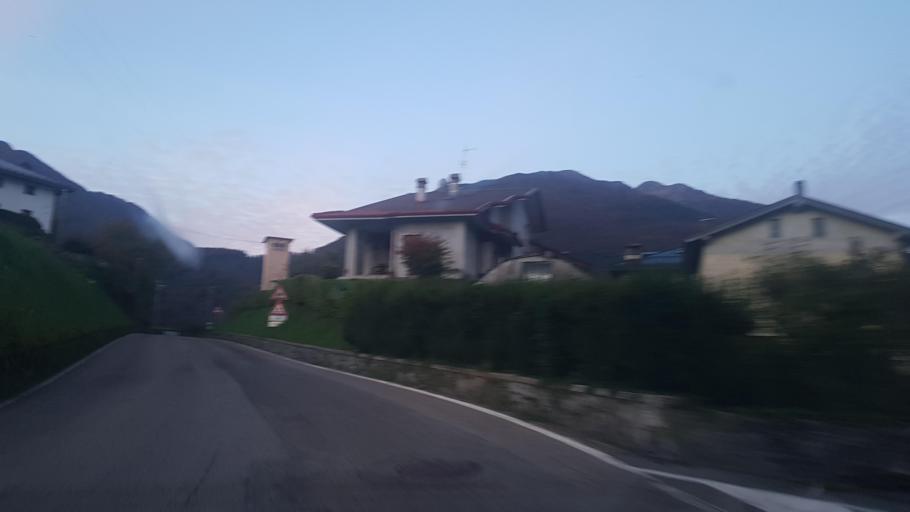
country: IT
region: Friuli Venezia Giulia
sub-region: Provincia di Udine
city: Chiaulis
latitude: 46.3841
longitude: 12.9790
